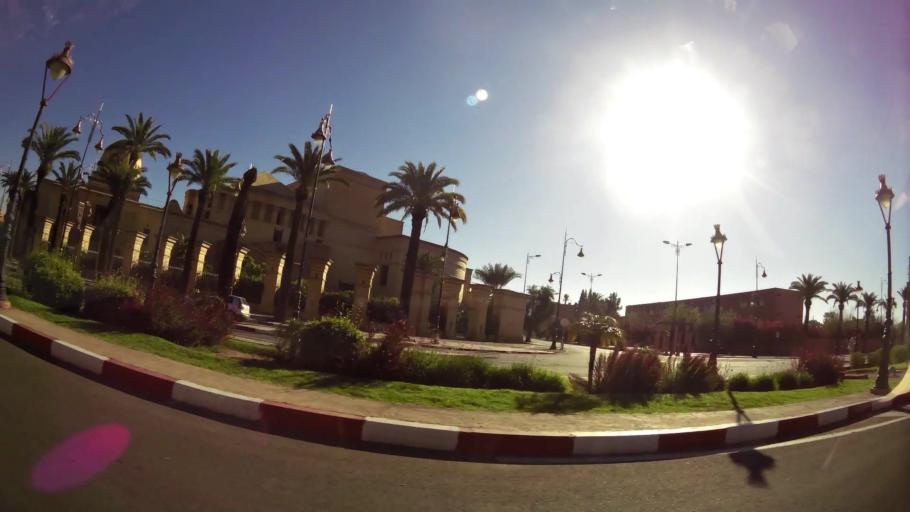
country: MA
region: Marrakech-Tensift-Al Haouz
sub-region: Marrakech
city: Marrakesh
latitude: 31.6290
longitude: -8.0154
